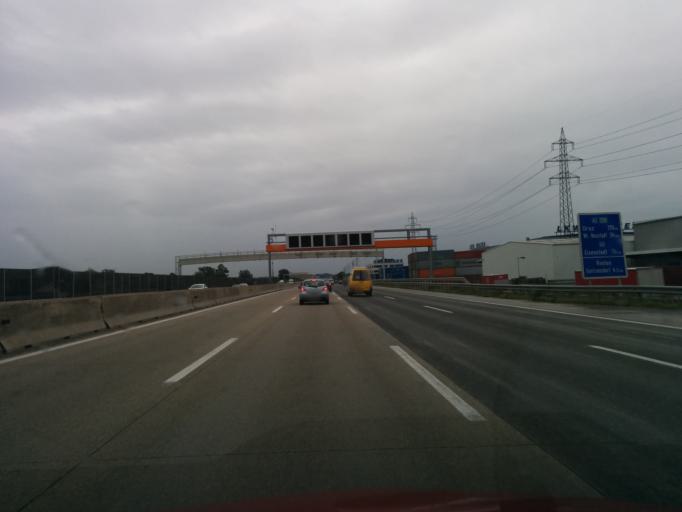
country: AT
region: Lower Austria
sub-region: Politischer Bezirk Modling
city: Biedermannsdorf
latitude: 48.0709
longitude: 16.3382
